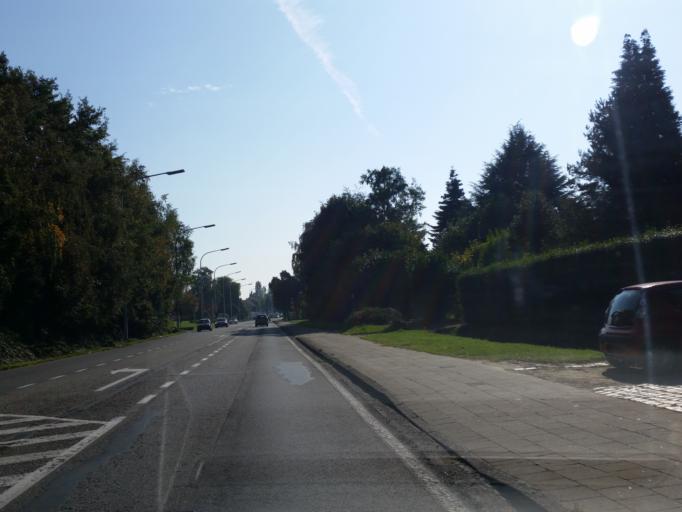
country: BE
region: Flanders
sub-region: Provincie Antwerpen
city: Kontich
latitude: 51.1393
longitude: 4.4574
